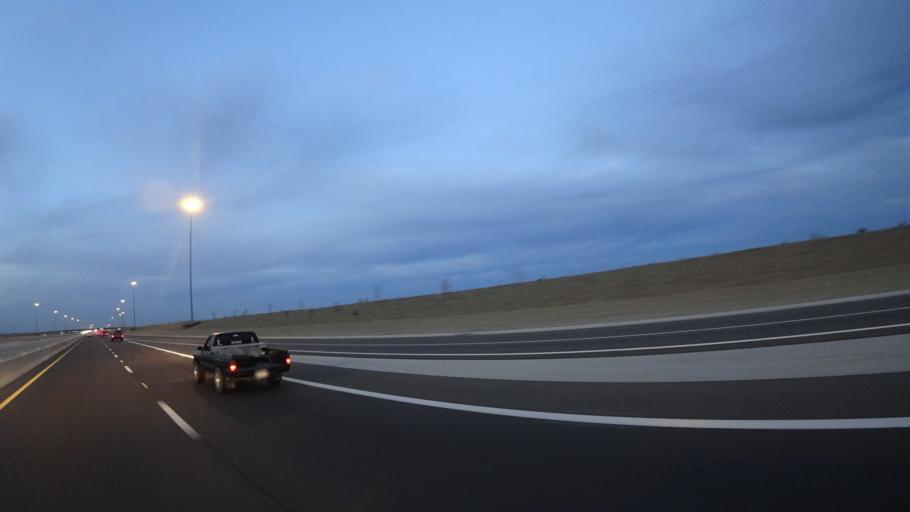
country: US
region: Arizona
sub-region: Maricopa County
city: Litchfield Park
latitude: 33.4711
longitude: -112.4256
